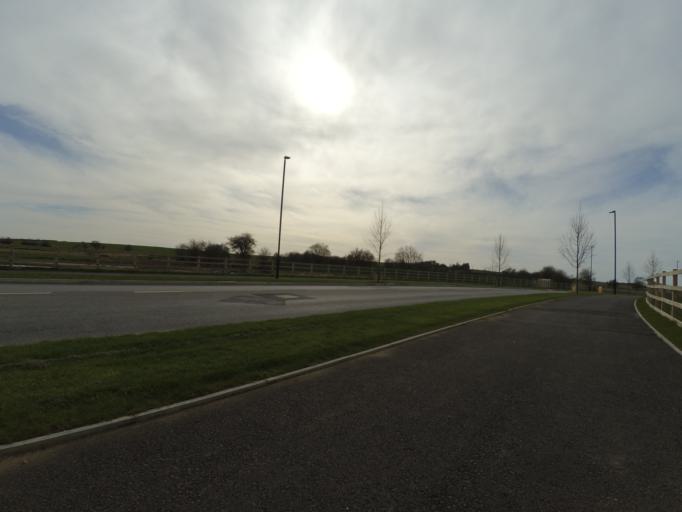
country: GB
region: England
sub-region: Warwickshire
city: Rugby
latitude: 52.3651
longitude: -1.1961
